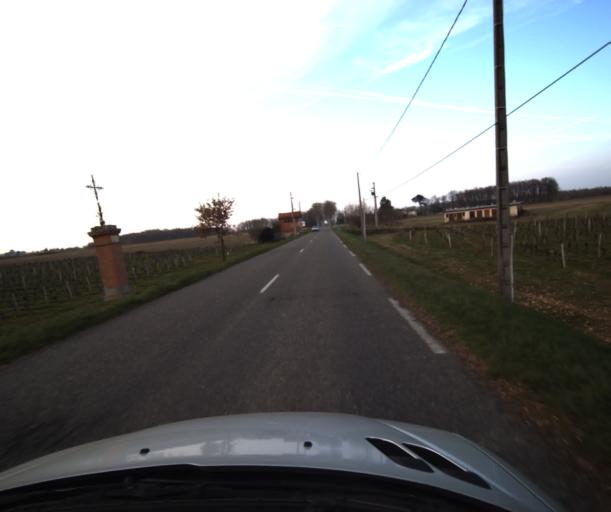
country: FR
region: Midi-Pyrenees
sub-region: Departement de la Haute-Garonne
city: Fronton
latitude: 43.8759
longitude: 1.3785
